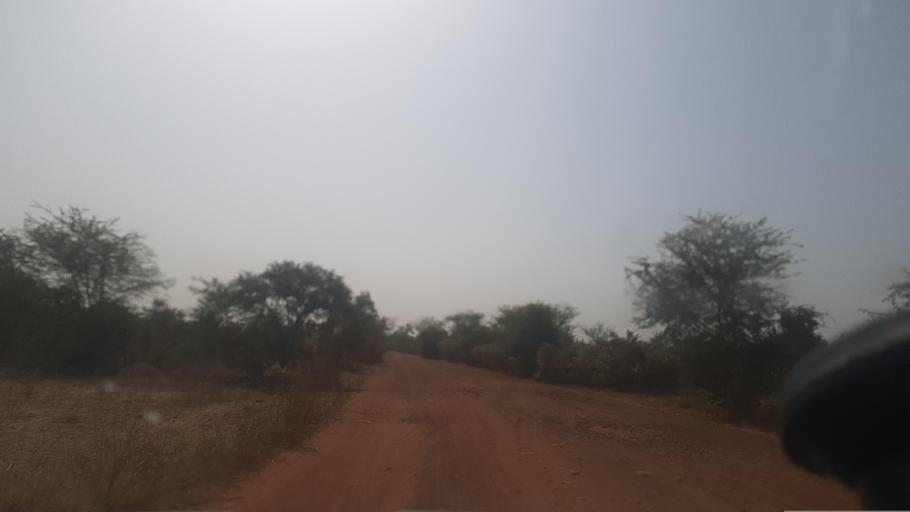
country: ML
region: Segou
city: Baroueli
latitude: 13.1403
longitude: -6.5132
